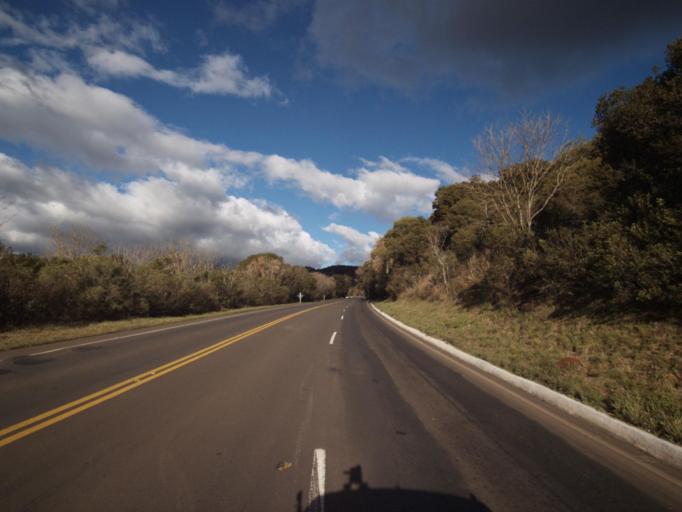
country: BR
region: Santa Catarina
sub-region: Joacaba
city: Joacaba
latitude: -27.2931
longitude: -51.4121
